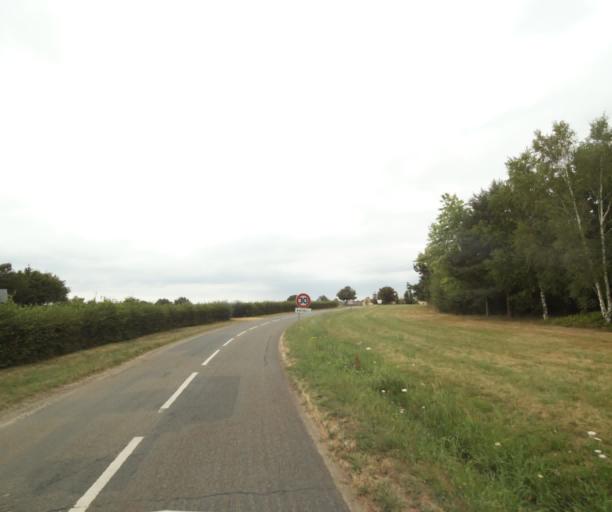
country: FR
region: Pays de la Loire
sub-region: Departement de la Sarthe
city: Sable-sur-Sarthe
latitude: 47.8180
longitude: -0.3531
